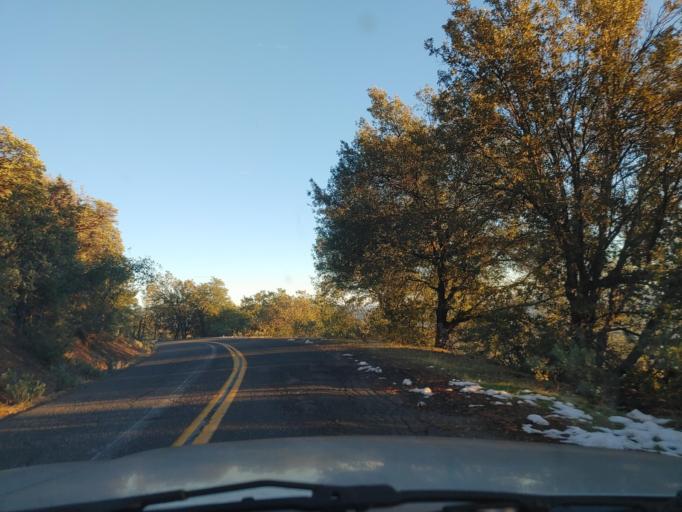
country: US
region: California
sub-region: Tuolumne County
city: Cedar Ridge
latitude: 38.0431
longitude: -120.3288
